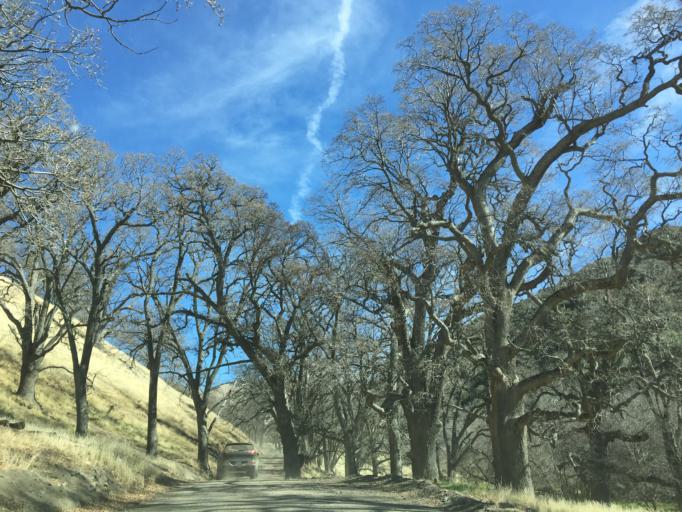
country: US
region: California
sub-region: Kern County
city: Lebec
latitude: 34.9111
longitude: -118.7040
